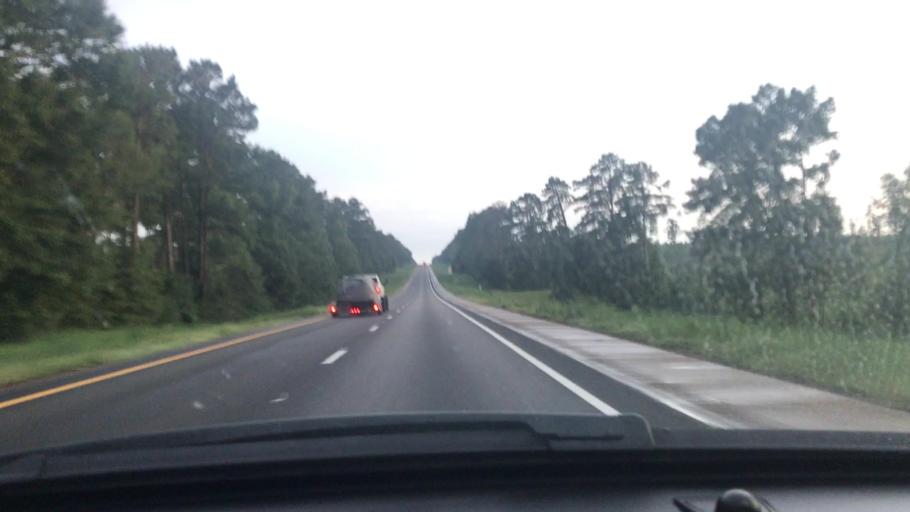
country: US
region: Mississippi
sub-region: Pike County
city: Magnolia
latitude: 31.0580
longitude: -90.4945
